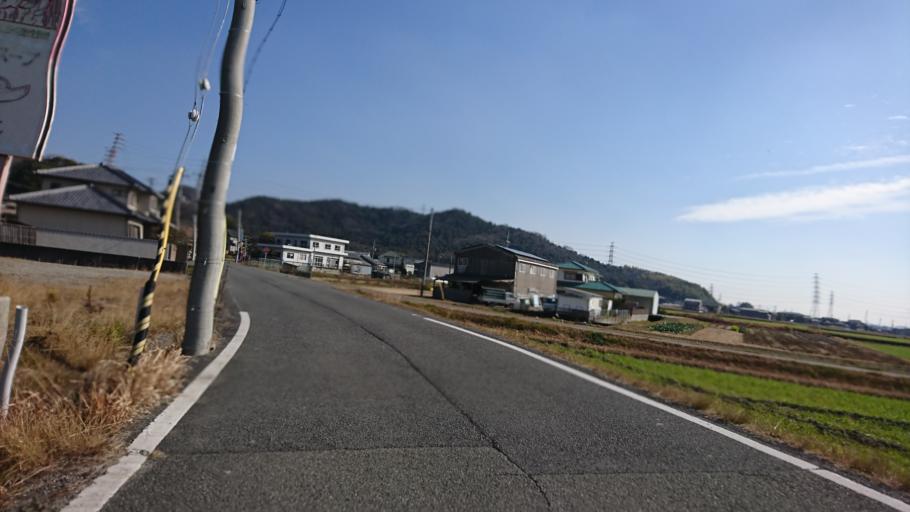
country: JP
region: Hyogo
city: Kakogawacho-honmachi
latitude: 34.8203
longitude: 134.8512
